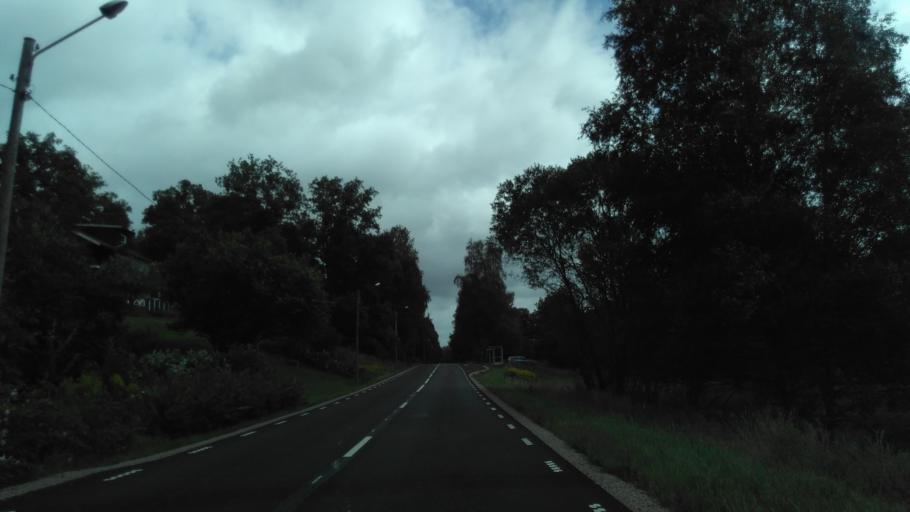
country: SE
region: Vaestra Goetaland
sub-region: Boras Kommun
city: Viskafors
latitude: 57.6130
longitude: 12.8027
